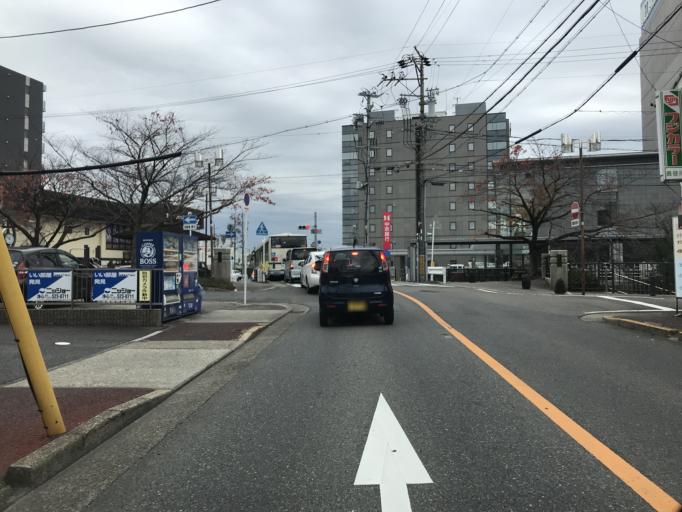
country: JP
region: Aichi
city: Nagoya-shi
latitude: 35.1917
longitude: 136.8775
